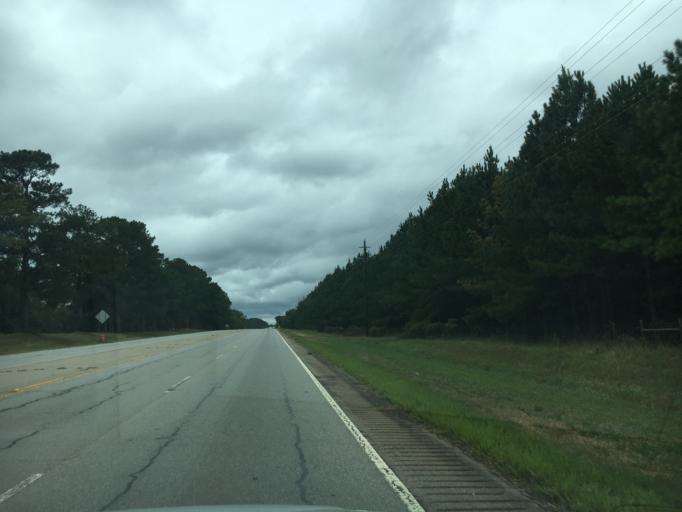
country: US
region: Georgia
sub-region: Wilkes County
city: Washington
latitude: 33.7028
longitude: -82.6920
